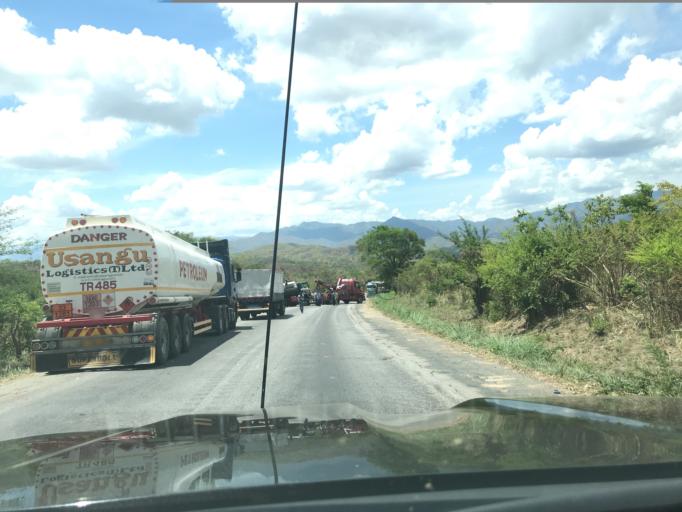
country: TZ
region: Morogoro
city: Mikumi
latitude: -7.4982
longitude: 36.8732
